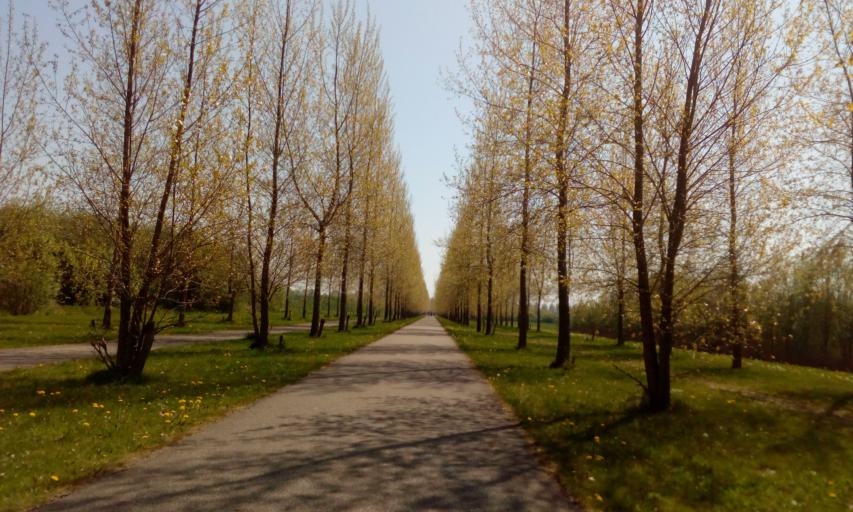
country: NL
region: South Holland
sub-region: Gemeente Hillegom
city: Hillegom
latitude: 52.2613
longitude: 4.6105
